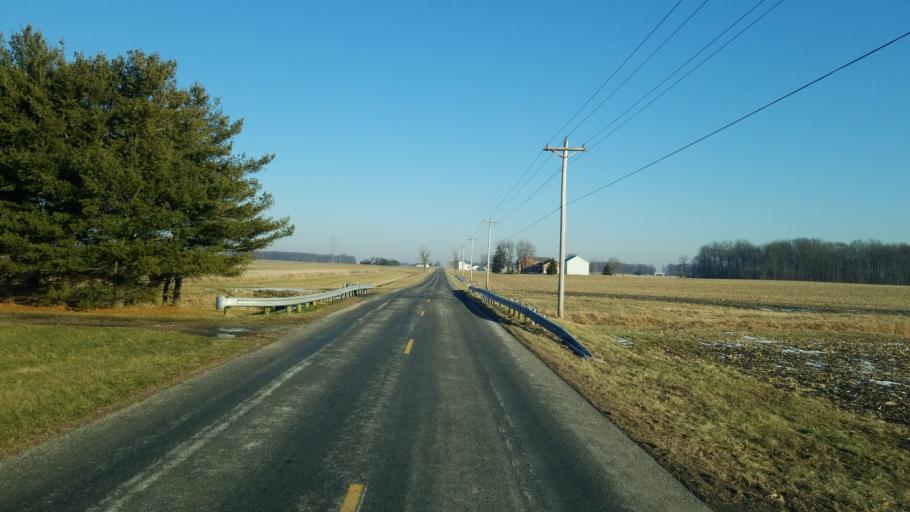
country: US
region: Ohio
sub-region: Crawford County
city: Bucyrus
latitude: 40.9648
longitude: -82.9527
